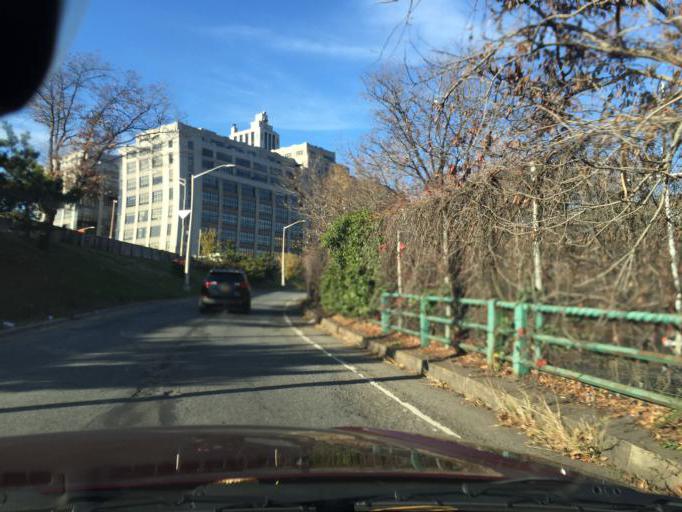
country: US
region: New York
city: New York City
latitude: 40.6918
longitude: -73.9989
